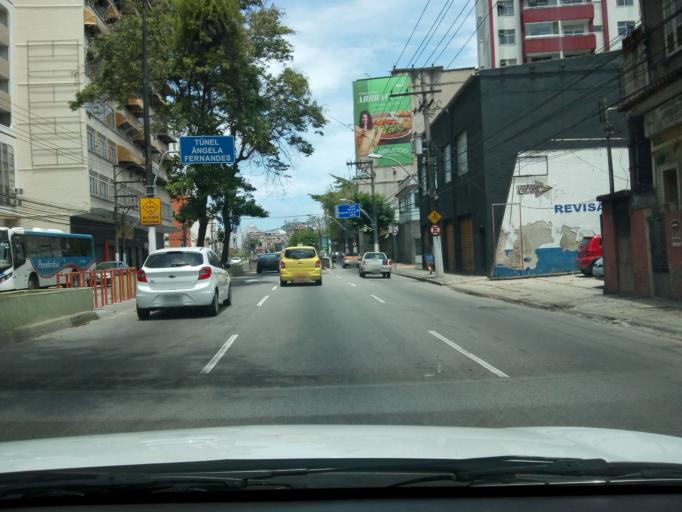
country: BR
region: Rio de Janeiro
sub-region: Niteroi
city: Niteroi
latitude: -22.8926
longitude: -43.1137
